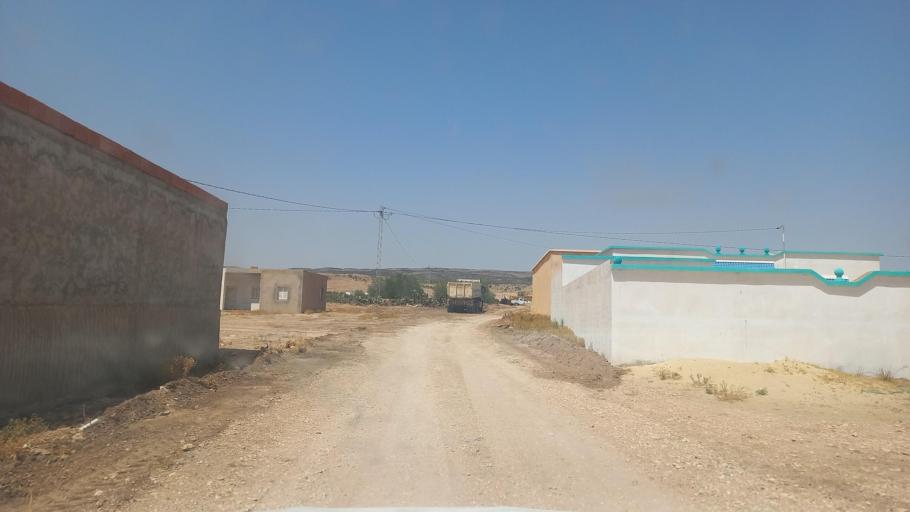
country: TN
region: Al Qasrayn
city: Kasserine
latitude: 35.2948
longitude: 8.9445
